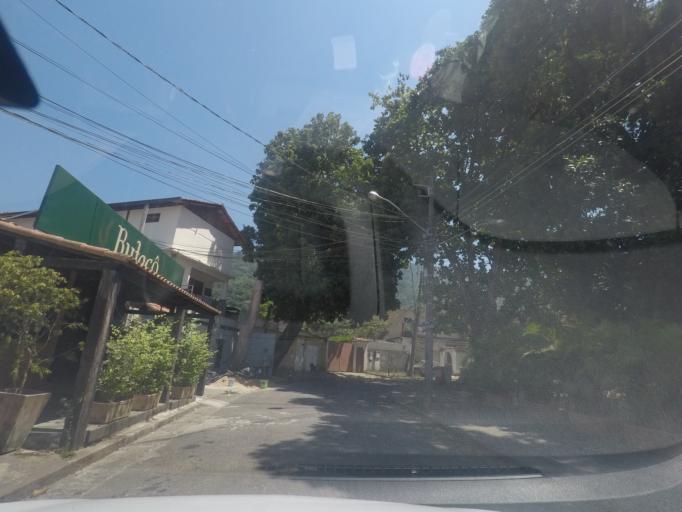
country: BR
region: Rio de Janeiro
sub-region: Nilopolis
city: Nilopolis
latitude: -22.9812
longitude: -43.4613
